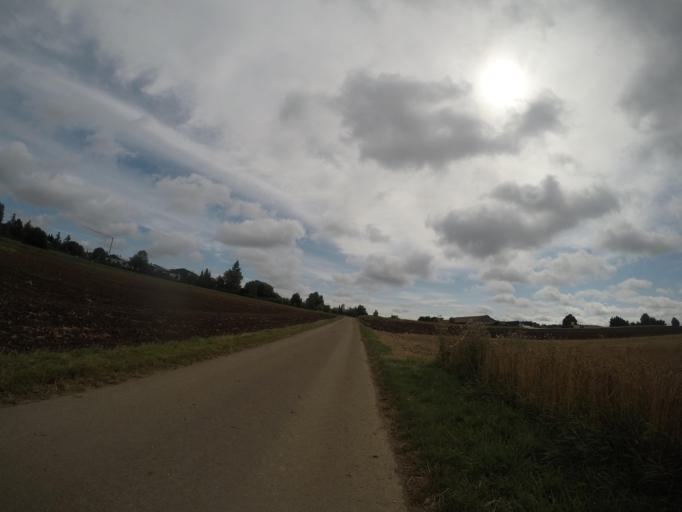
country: DE
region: Baden-Wuerttemberg
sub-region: Tuebingen Region
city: Westerheim
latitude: 48.4771
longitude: 9.6182
